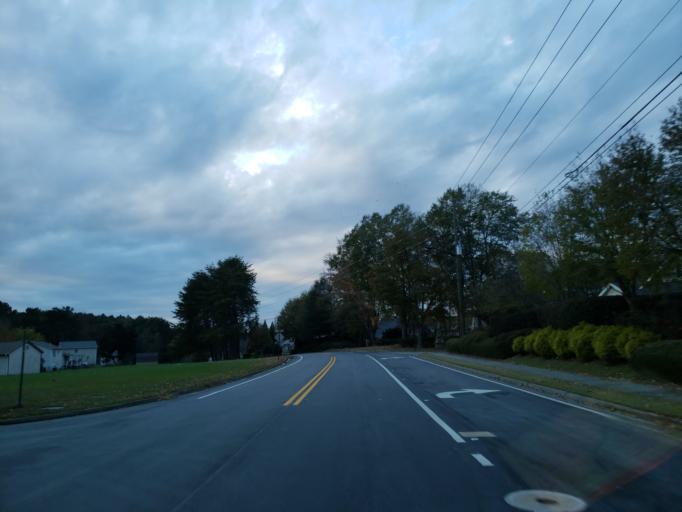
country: US
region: Georgia
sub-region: Cobb County
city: Acworth
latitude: 34.0330
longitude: -84.6882
